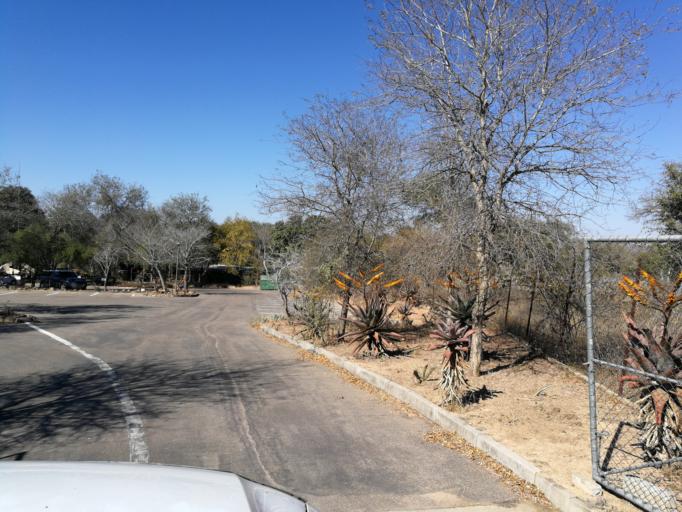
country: ZA
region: Limpopo
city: Thulamahashi
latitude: -24.9839
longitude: 31.5766
